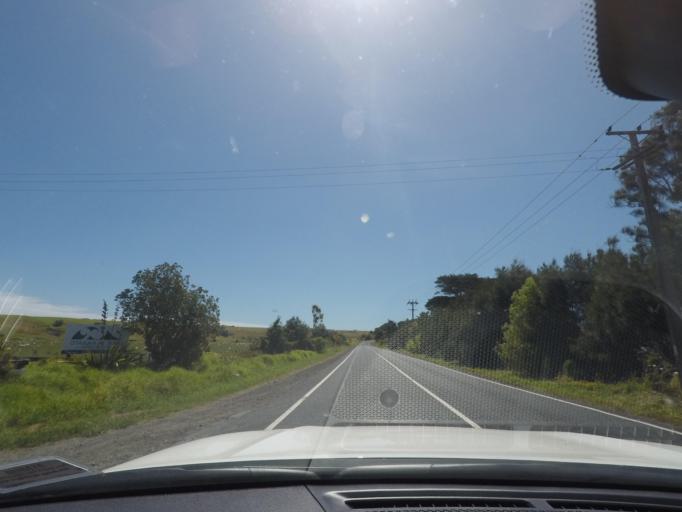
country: NZ
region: Auckland
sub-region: Auckland
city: Parakai
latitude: -36.6357
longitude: 174.3824
